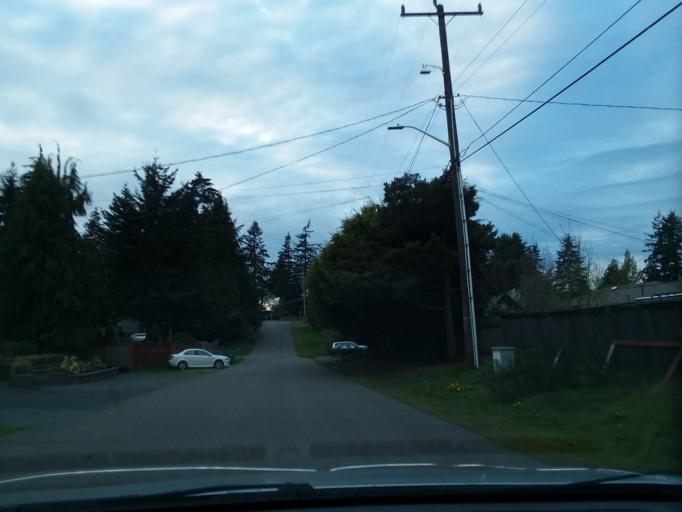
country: US
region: Washington
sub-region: Snohomish County
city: Esperance
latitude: 47.7760
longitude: -122.3490
